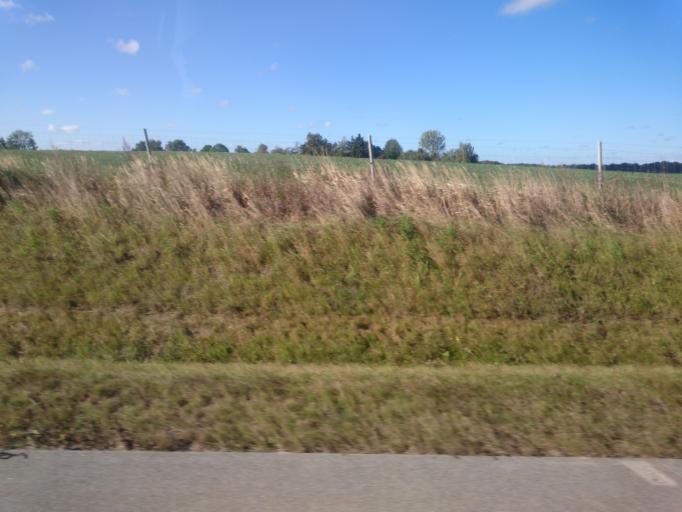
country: DE
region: Mecklenburg-Vorpommern
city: Dummerstorf
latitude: 53.9119
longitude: 12.2393
